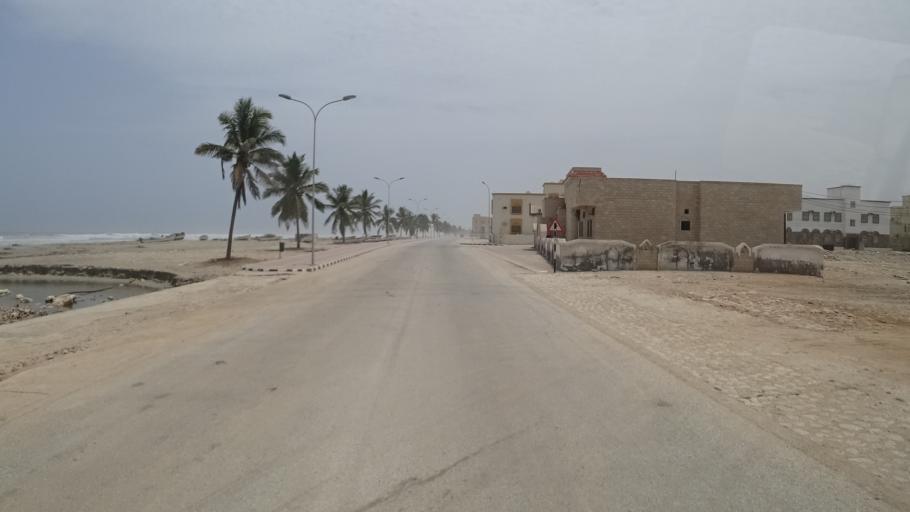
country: OM
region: Zufar
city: Salalah
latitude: 17.0346
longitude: 54.4027
